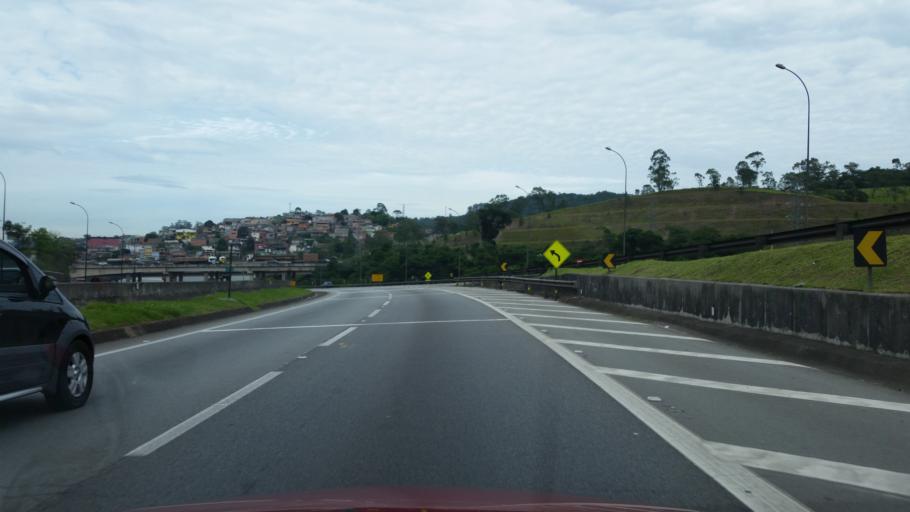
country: BR
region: Sao Paulo
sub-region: Embu
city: Embu
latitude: -23.6358
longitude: -46.8308
